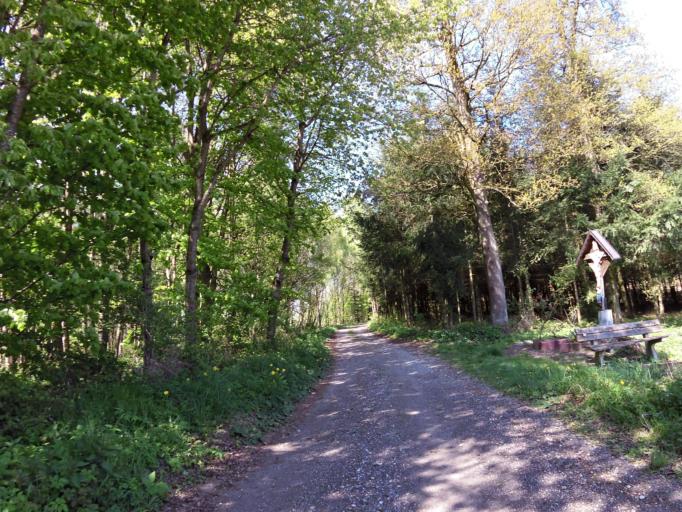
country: DE
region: Bavaria
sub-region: Upper Bavaria
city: Fraunberg
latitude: 48.3392
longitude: 12.0066
